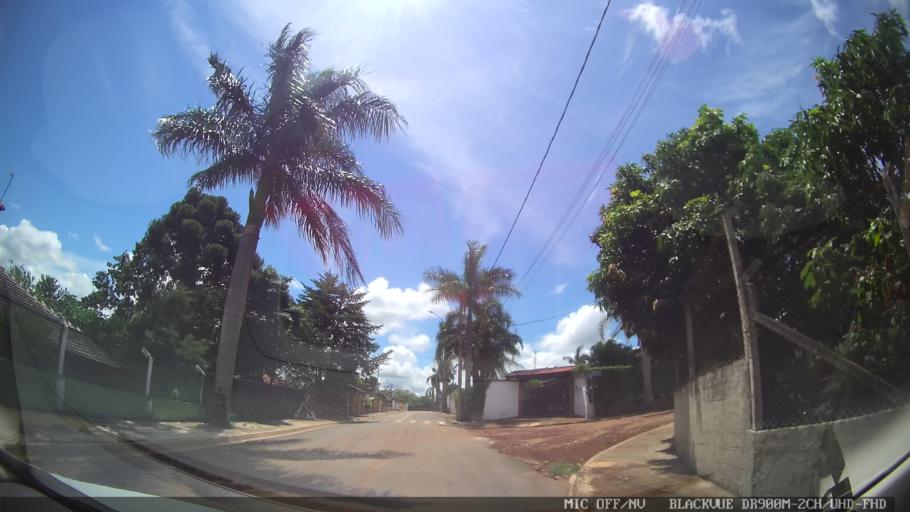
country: BR
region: Sao Paulo
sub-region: Amparo
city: Amparo
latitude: -22.8186
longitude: -46.6917
